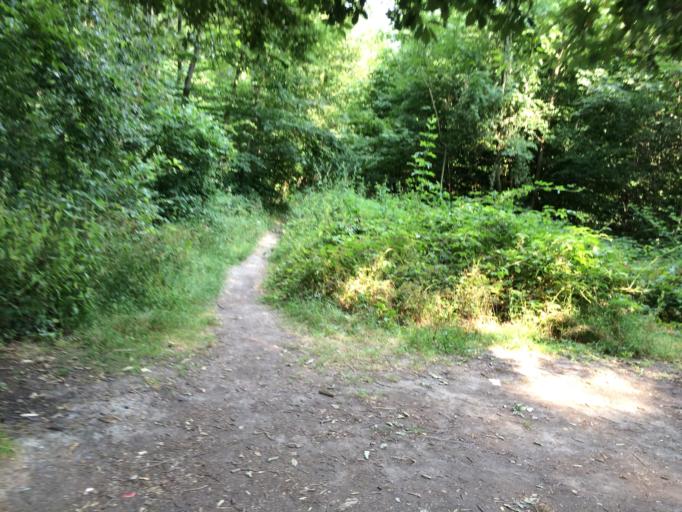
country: FR
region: Ile-de-France
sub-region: Departement de l'Essonne
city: Bievres
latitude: 48.7747
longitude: 2.2324
